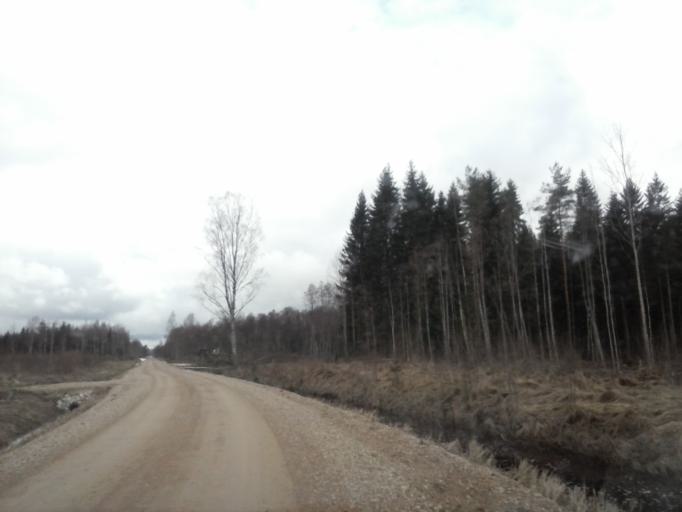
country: EE
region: Jogevamaa
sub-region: Mustvee linn
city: Mustvee
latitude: 59.0941
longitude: 26.8594
